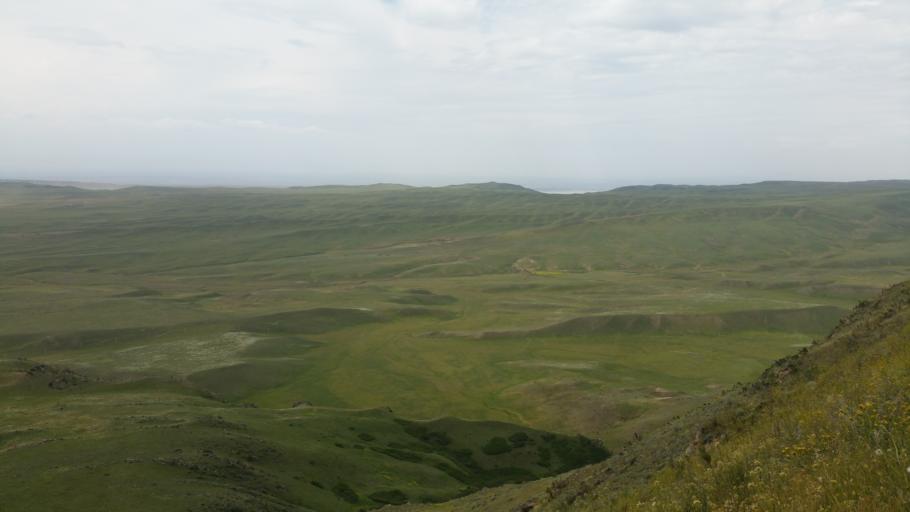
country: AZ
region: Agstafa
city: Saloglu
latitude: 41.4432
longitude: 45.3750
